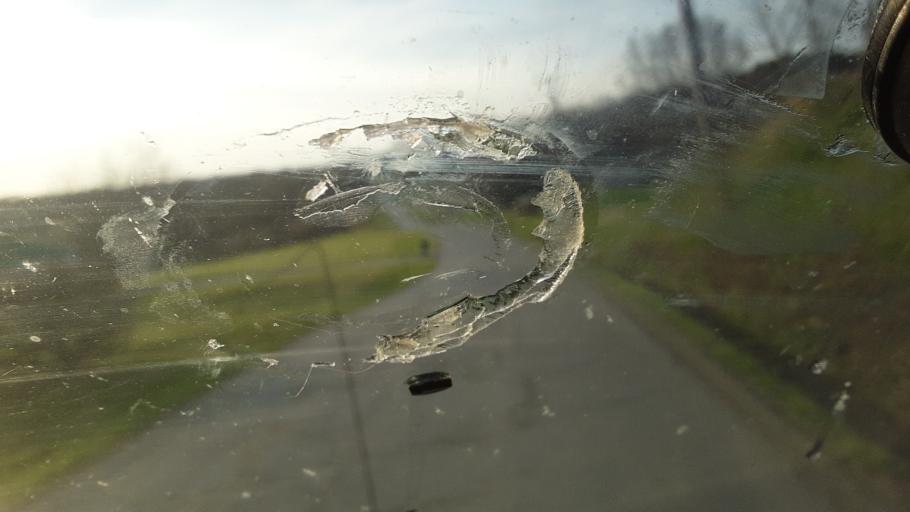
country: US
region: Ohio
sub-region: Richland County
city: Lincoln Heights
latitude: 40.7204
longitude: -82.4386
